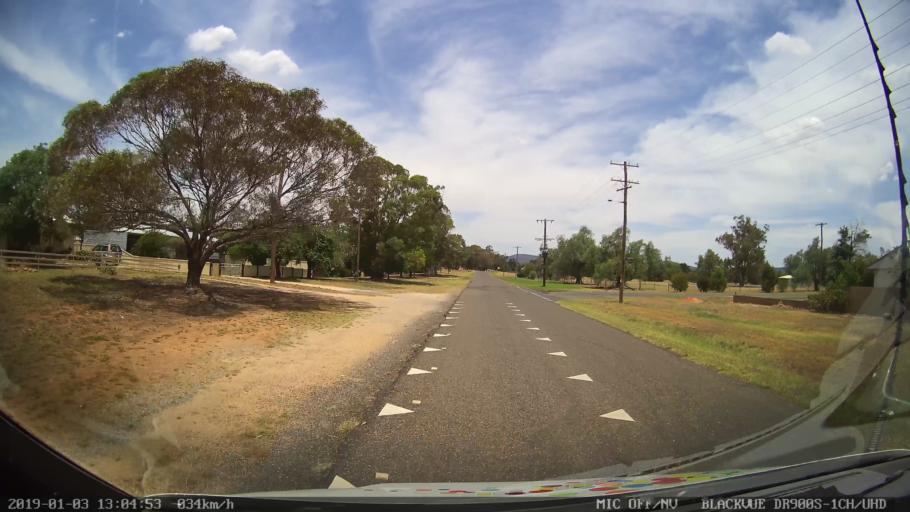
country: AU
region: New South Wales
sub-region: Cabonne
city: Canowindra
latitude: -33.6161
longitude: 148.4390
